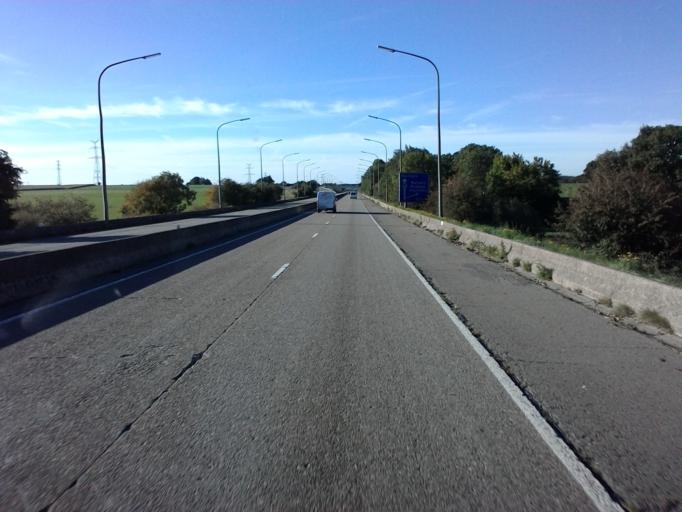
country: BE
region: Wallonia
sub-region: Province du Luxembourg
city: Martelange
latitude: 49.8594
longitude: 5.7248
